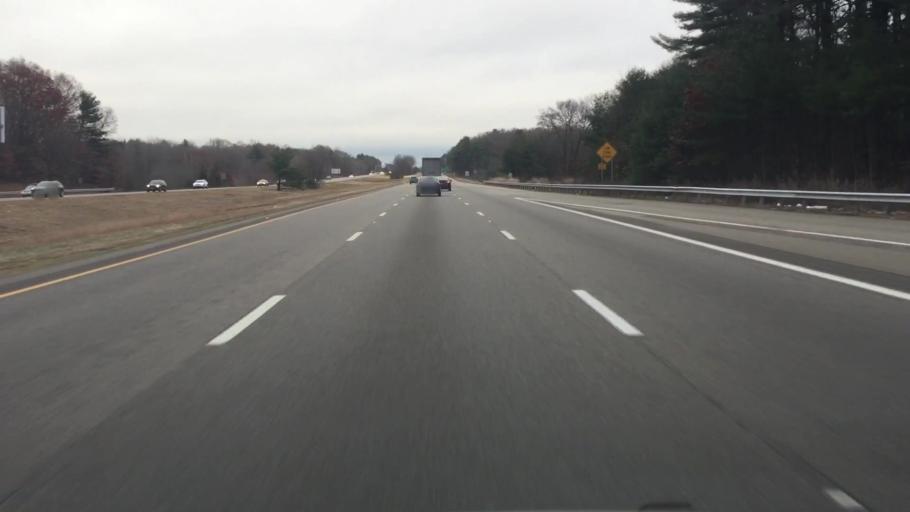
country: US
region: Massachusetts
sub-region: Bristol County
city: Mansfield Center
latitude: 41.9994
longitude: -71.2070
